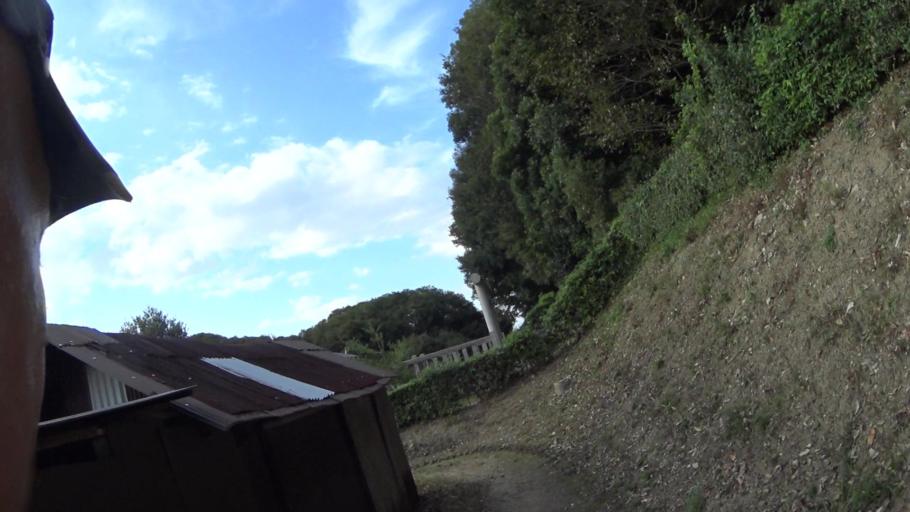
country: JP
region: Nara
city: Sakurai
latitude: 34.5384
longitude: 135.8393
